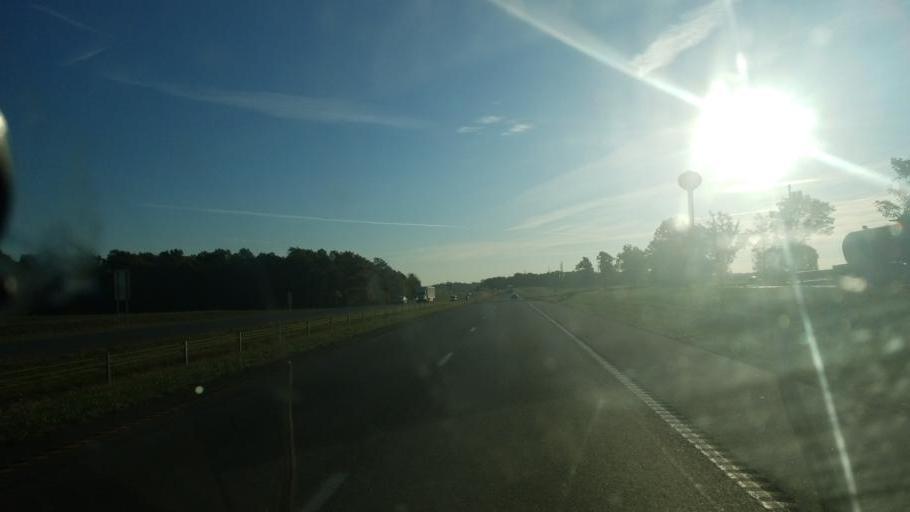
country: US
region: Missouri
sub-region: Warren County
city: Warrenton
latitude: 38.8467
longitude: -91.2702
